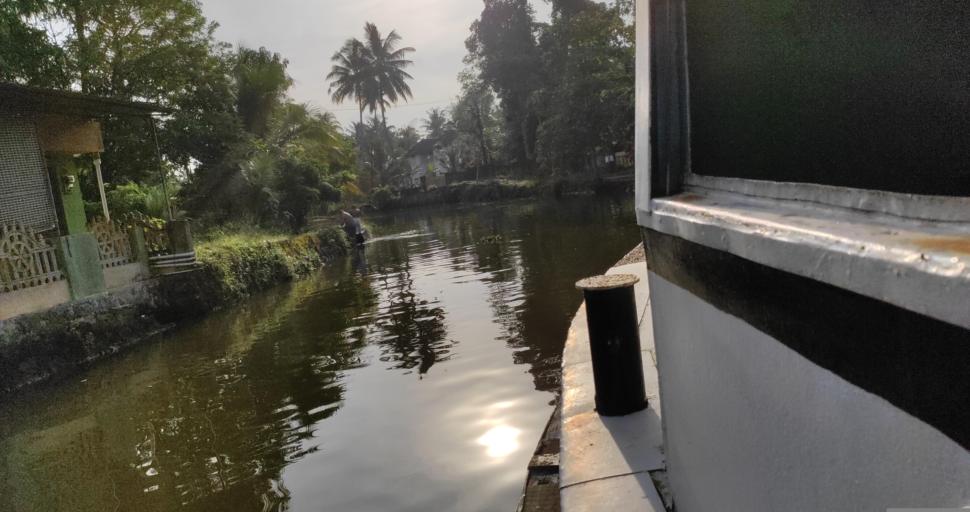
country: IN
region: Kerala
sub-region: Kottayam
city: Kottayam
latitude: 9.5967
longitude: 76.4284
